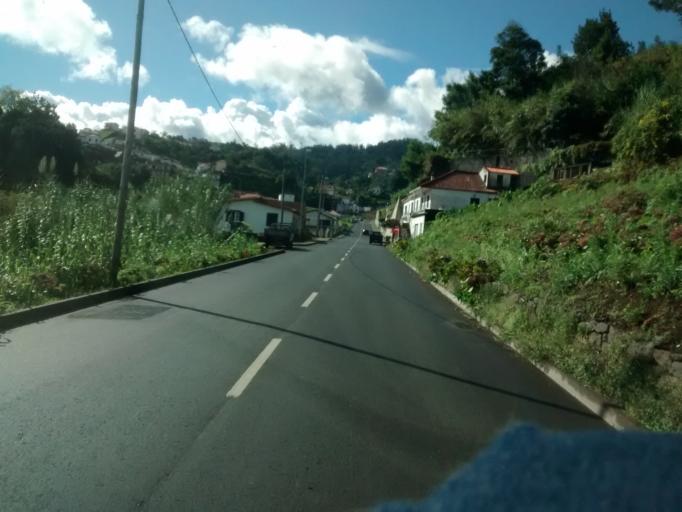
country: PT
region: Madeira
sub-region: Santana
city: Santana
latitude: 32.8084
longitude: -16.8846
